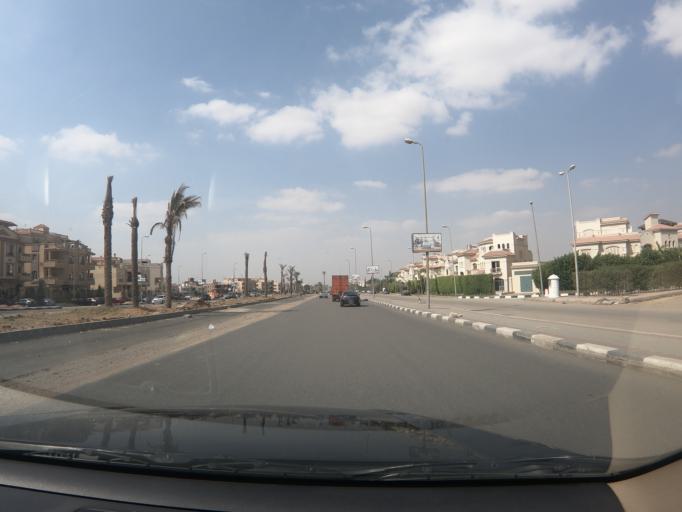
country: EG
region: Muhafazat al Qalyubiyah
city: Al Khankah
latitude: 30.0524
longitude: 31.4751
